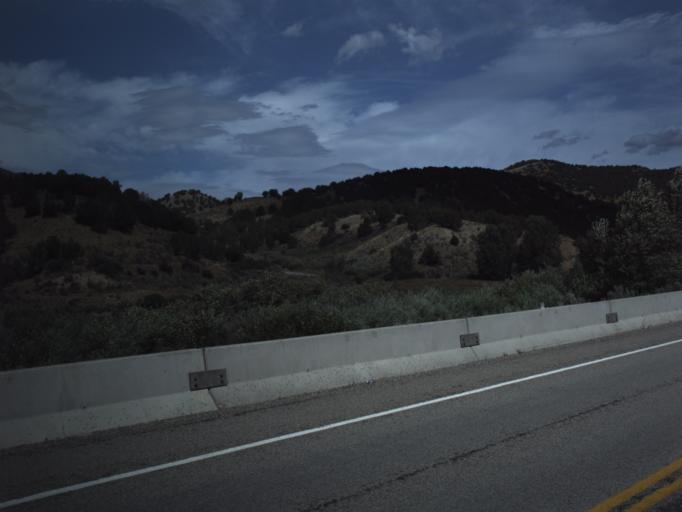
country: US
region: Utah
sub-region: Utah County
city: Woodland Hills
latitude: 39.9476
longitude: -111.5386
